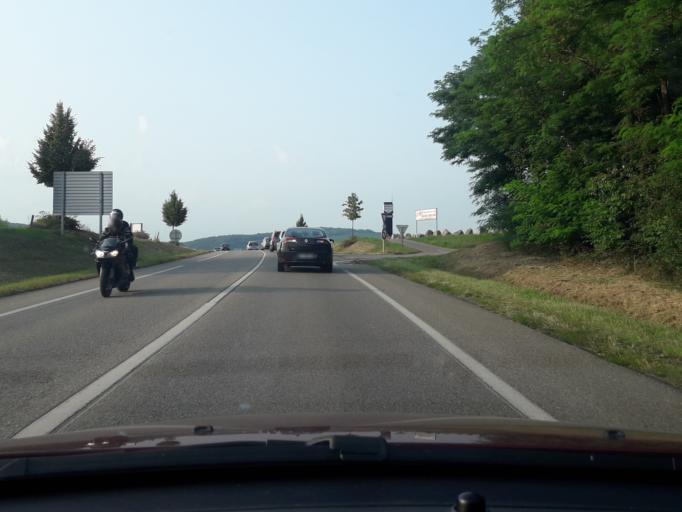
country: FR
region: Alsace
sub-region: Departement du Bas-Rhin
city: Irmstett
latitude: 48.6009
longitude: 7.4811
